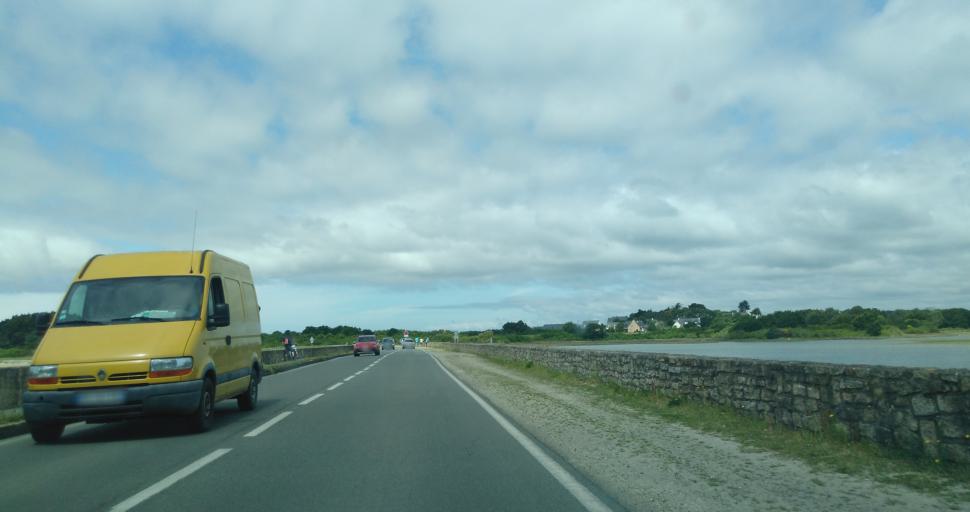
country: FR
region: Brittany
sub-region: Departement du Morbihan
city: La Trinite-sur-Mer
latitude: 47.5788
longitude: -3.0389
